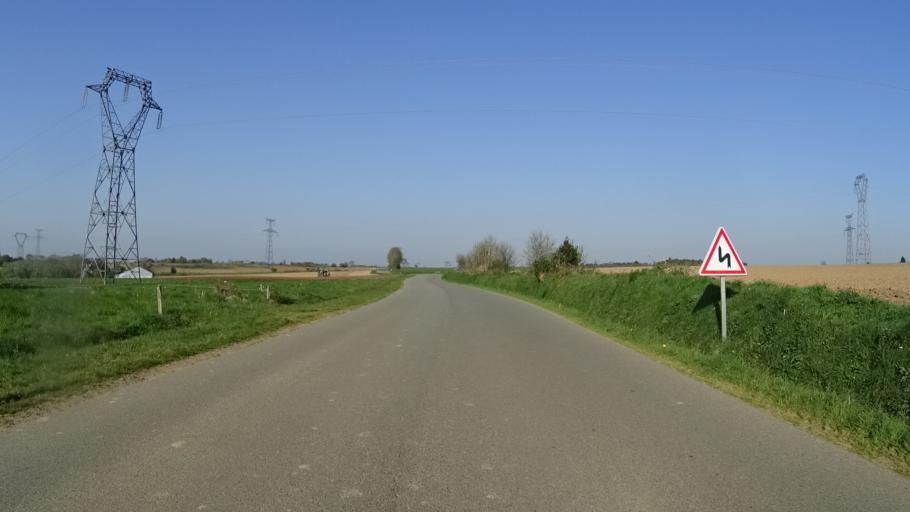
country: FR
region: Brittany
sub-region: Departement du Finistere
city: Irvillac
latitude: 48.3843
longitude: -4.1686
